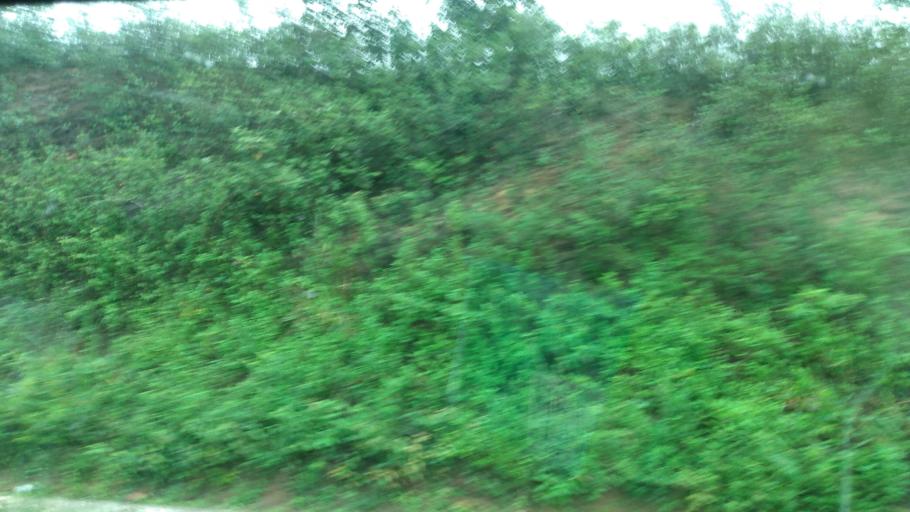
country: BR
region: Pernambuco
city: Garanhuns
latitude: -8.8775
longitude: -36.5096
